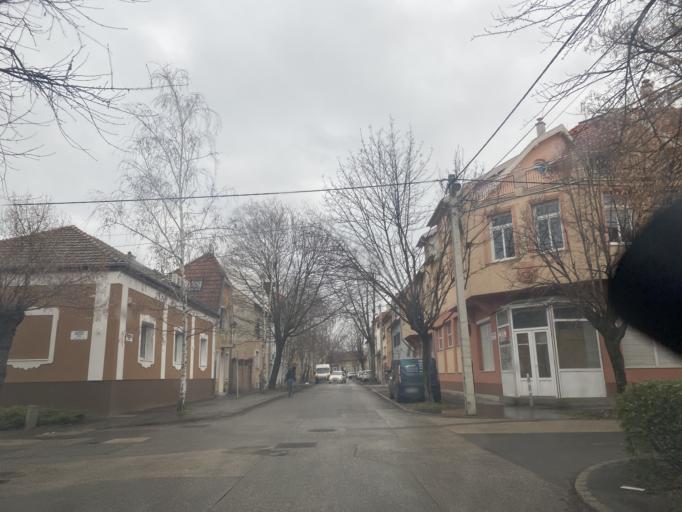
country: HU
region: Csongrad
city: Szeged
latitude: 46.2619
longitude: 20.1448
